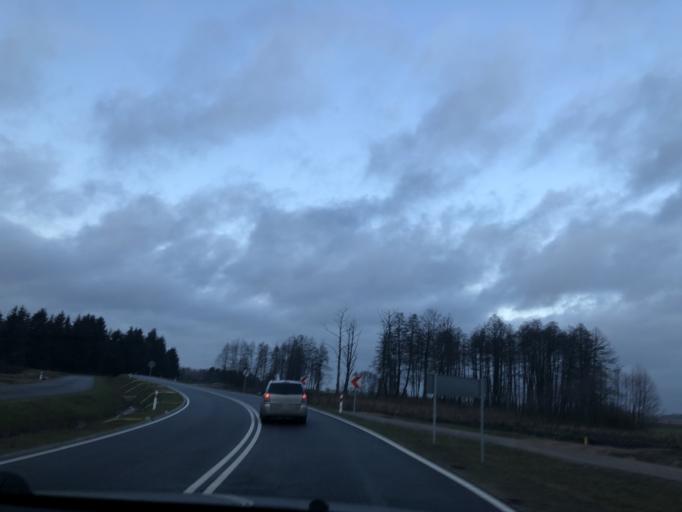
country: PL
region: Podlasie
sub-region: Lomza
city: Lomza
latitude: 53.1262
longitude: 22.0487
